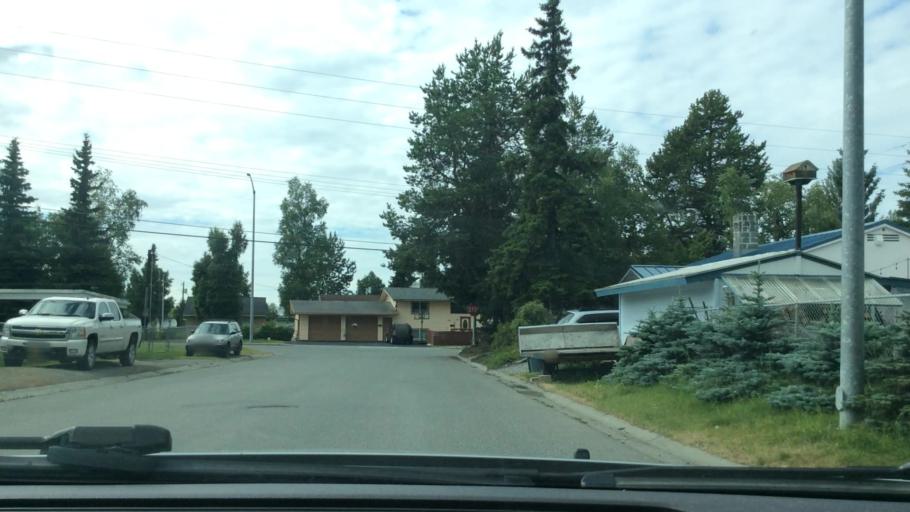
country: US
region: Alaska
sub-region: Anchorage Municipality
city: Anchorage
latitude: 61.2201
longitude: -149.7921
